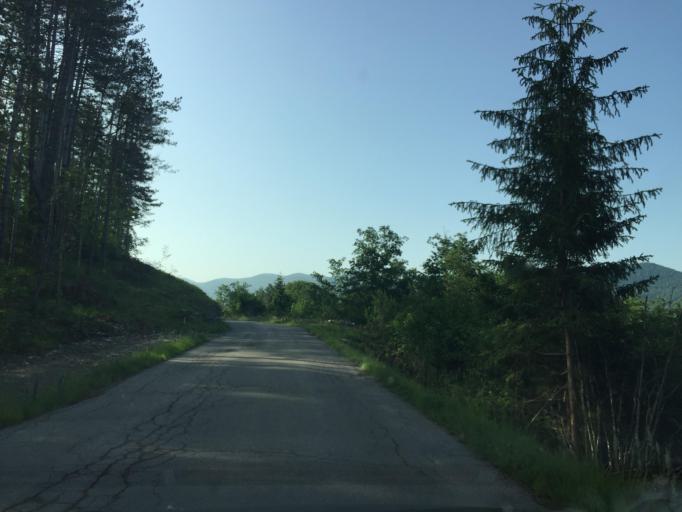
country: HR
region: Istarska
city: Buzet
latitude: 45.4567
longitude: 14.1430
